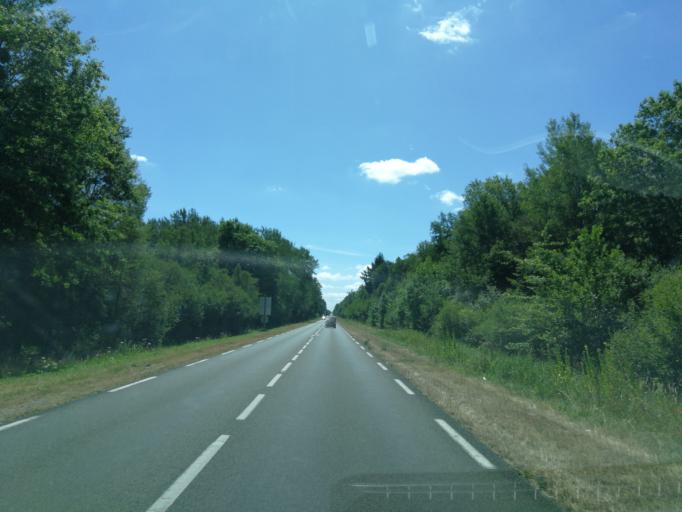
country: FR
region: Centre
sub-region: Departement du Loiret
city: La Ferte-Saint-Aubin
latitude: 47.6787
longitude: 1.9661
